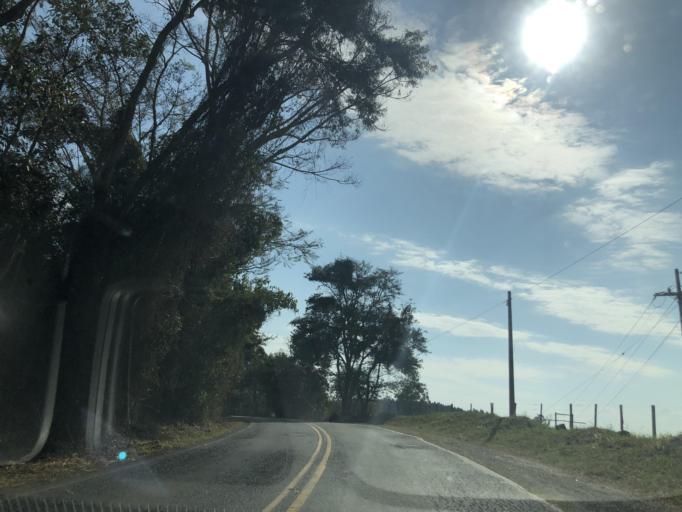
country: BR
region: Sao Paulo
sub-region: Pilar Do Sul
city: Pilar do Sul
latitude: -23.8270
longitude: -47.6765
